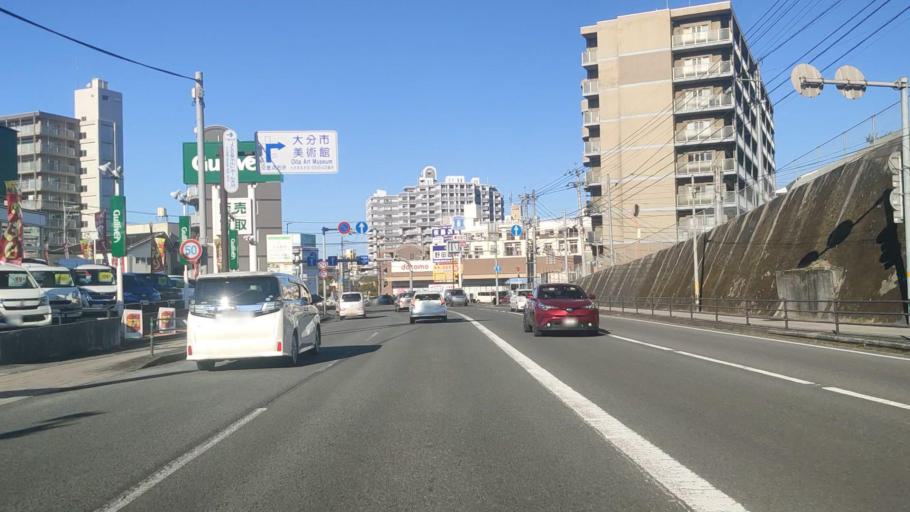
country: JP
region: Oita
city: Oita
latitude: 33.2240
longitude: 131.5954
